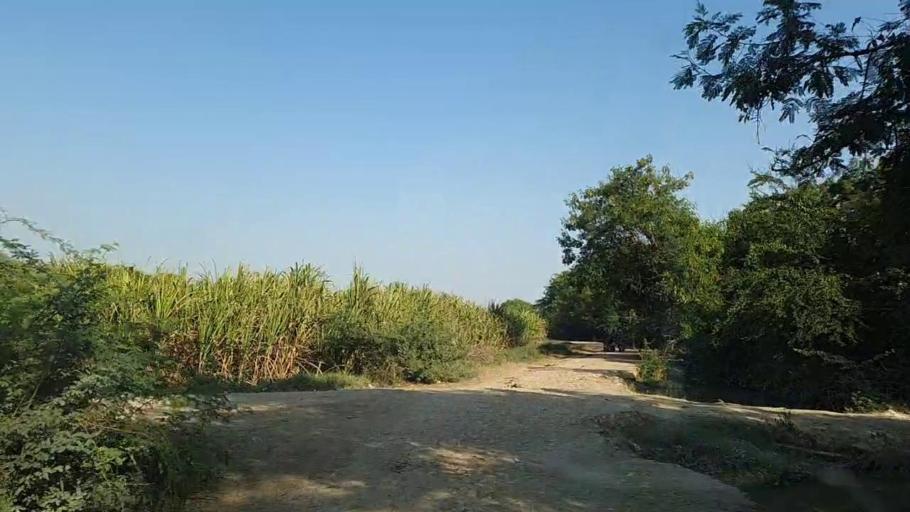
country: PK
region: Sindh
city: Chuhar Jamali
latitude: 24.5714
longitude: 68.0351
